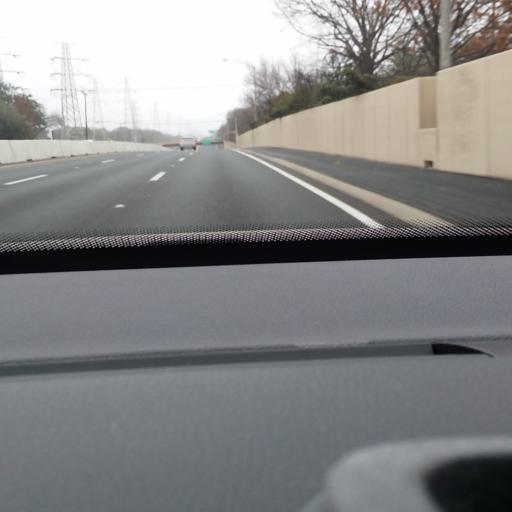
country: US
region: Texas
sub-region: Dallas County
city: University Park
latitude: 32.8820
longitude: -96.8024
